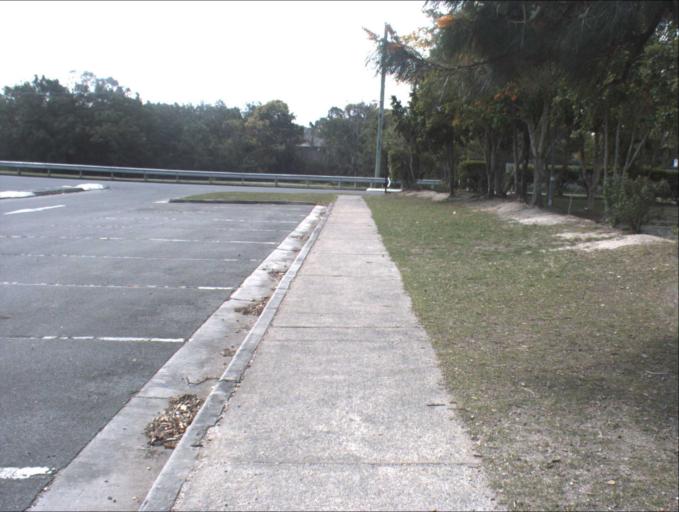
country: AU
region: Queensland
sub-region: Logan
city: Logan City
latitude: -27.6748
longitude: 153.0909
